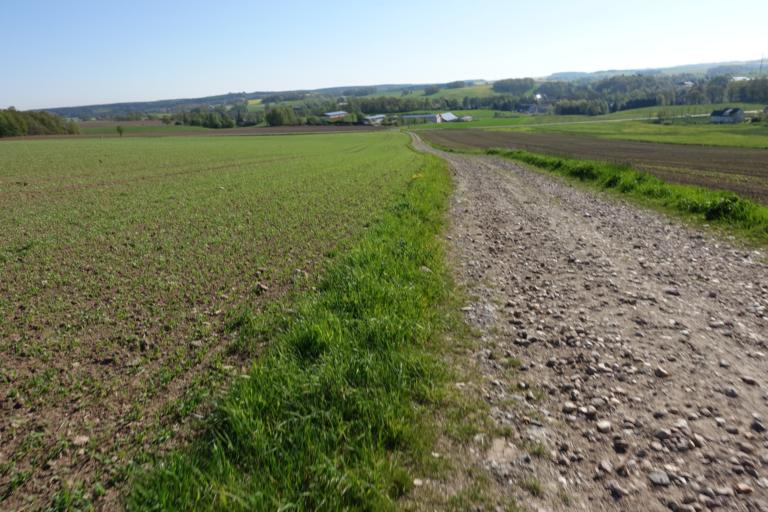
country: DE
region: Saxony
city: Lichtenberg
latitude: 50.9003
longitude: 13.4220
